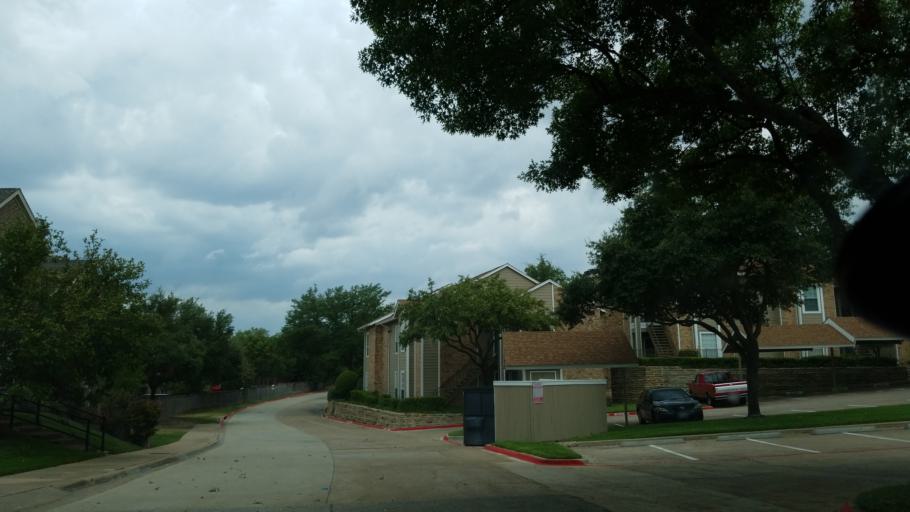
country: US
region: Texas
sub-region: Dallas County
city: Richardson
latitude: 32.8982
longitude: -96.7230
